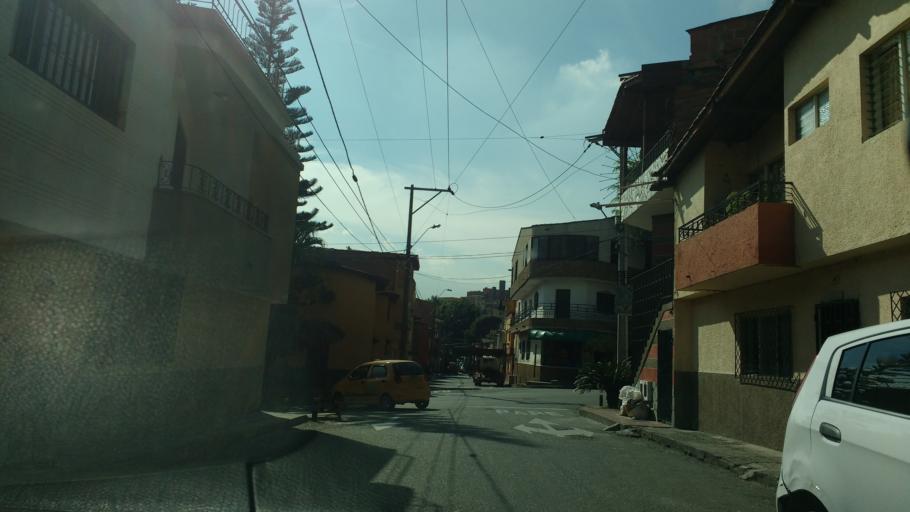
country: CO
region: Antioquia
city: Medellin
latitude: 6.2520
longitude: -75.5958
